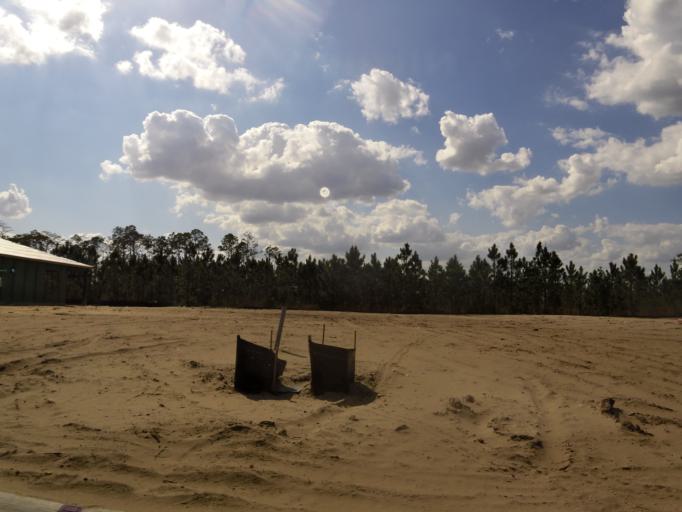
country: US
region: Florida
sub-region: Saint Johns County
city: Palm Valley
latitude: 30.1895
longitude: -81.5011
